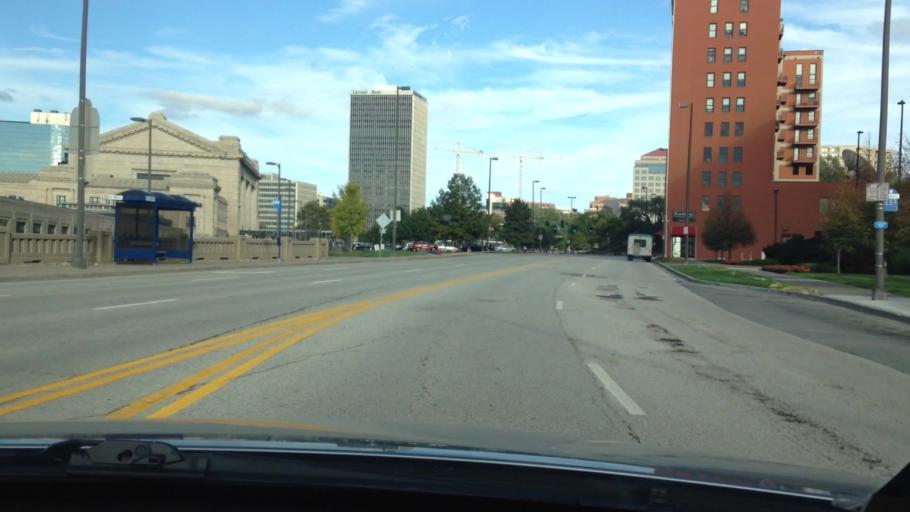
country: US
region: Missouri
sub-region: Jackson County
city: Kansas City
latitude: 39.0834
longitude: -94.5889
